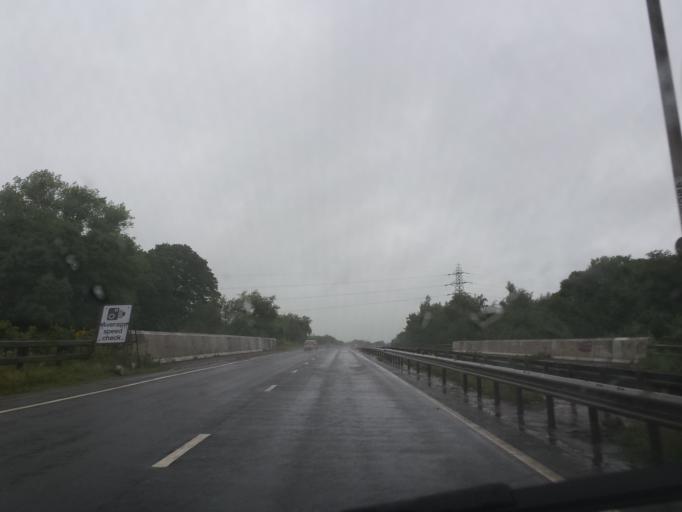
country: GB
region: England
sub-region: Warwickshire
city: Ryton on Dunsmore
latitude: 52.3866
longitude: -1.4442
